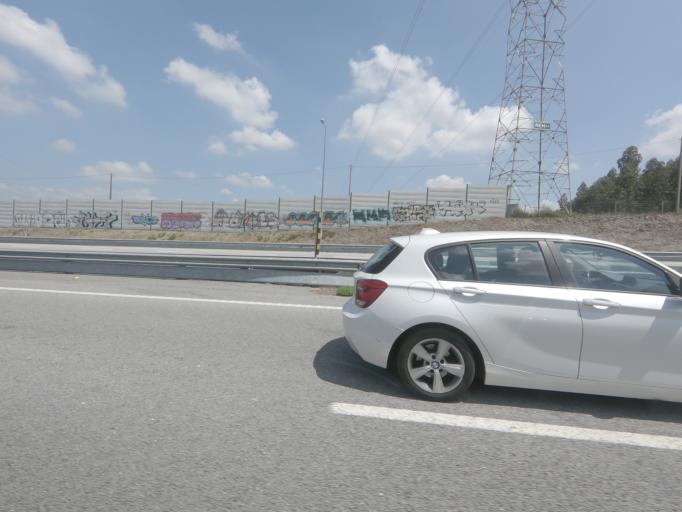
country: PT
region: Porto
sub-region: Valongo
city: Campo
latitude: 41.1808
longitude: -8.4460
